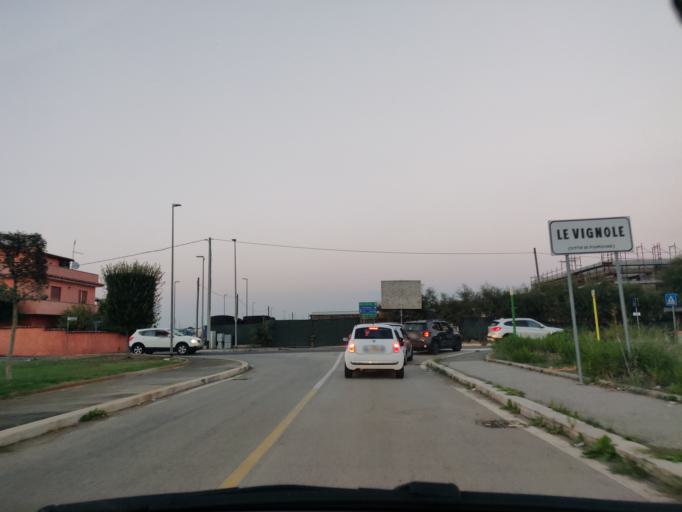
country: IT
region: Latium
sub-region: Citta metropolitana di Roma Capitale
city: Npp 23 (Parco Leonardo)
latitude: 41.8098
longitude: 12.3045
